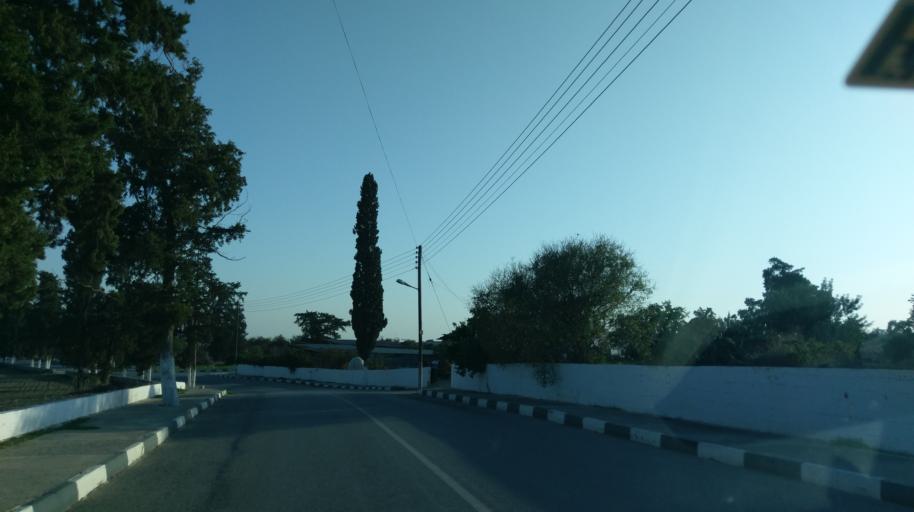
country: CY
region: Ammochostos
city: Leonarisso
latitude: 35.4076
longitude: 33.9938
